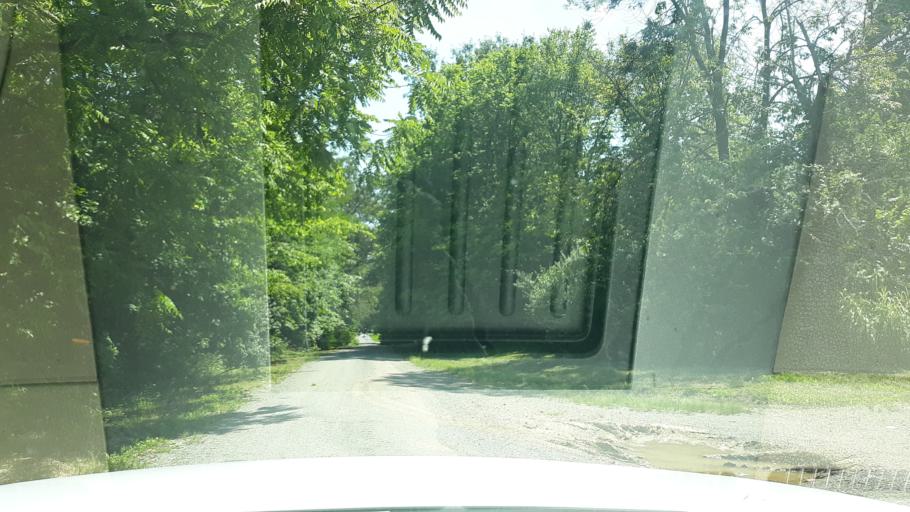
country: US
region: Illinois
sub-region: Saline County
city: Harrisburg
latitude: 37.8494
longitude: -88.6099
